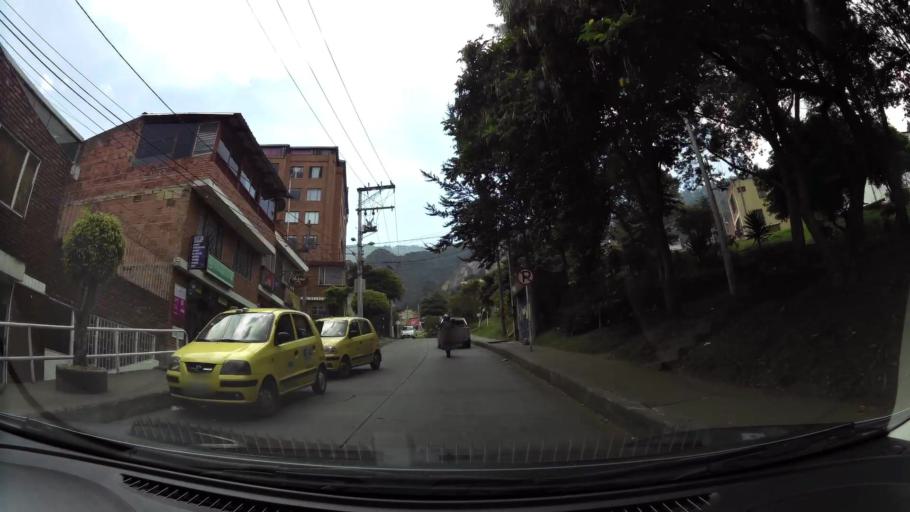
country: CO
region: Bogota D.C.
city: Barrio San Luis
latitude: 4.7051
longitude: -74.0241
